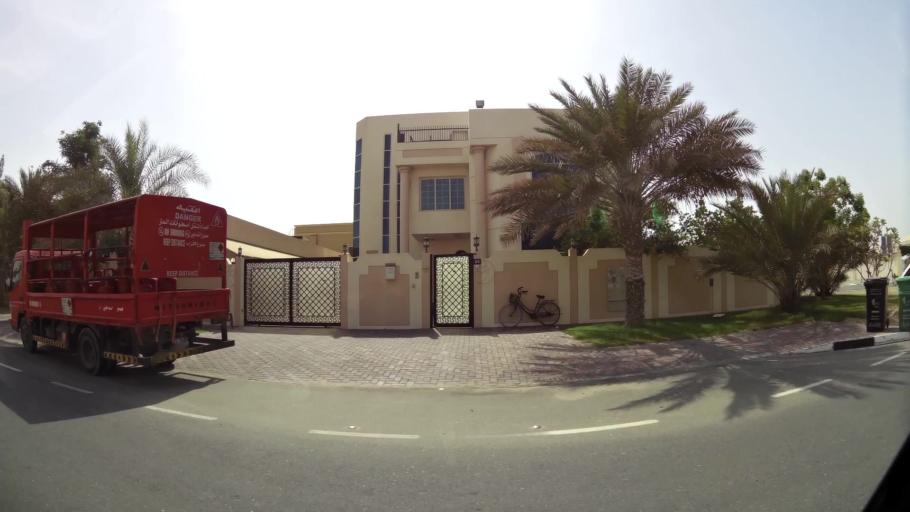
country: AE
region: Ash Shariqah
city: Sharjah
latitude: 25.2496
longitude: 55.4356
